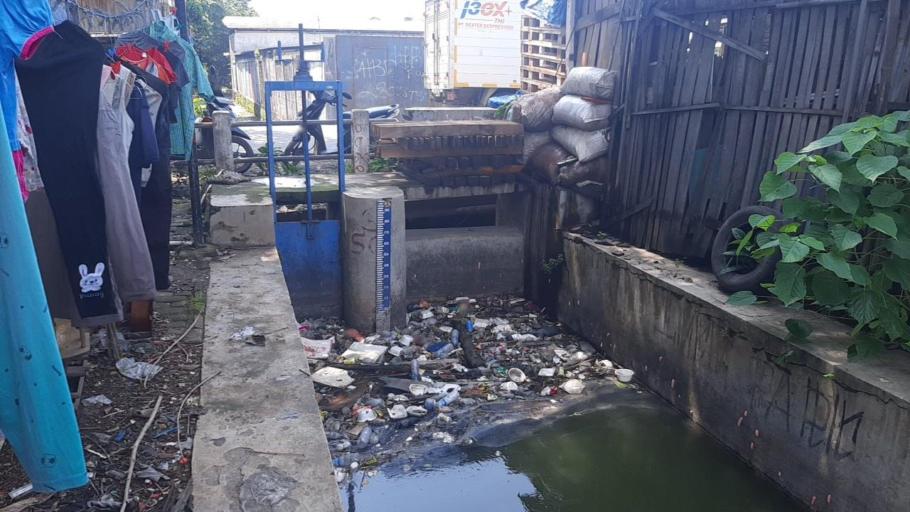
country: ID
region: West Java
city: Cileungsir
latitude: -6.4442
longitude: 106.9462
